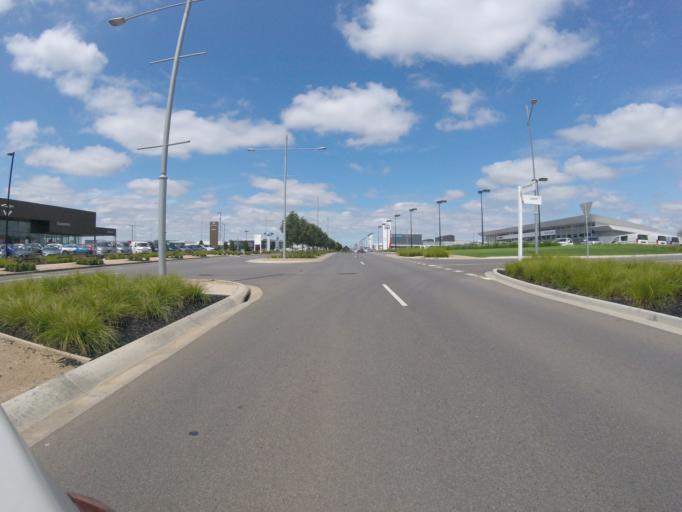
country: AU
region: Victoria
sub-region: Moreland
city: Gowanbrae
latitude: -37.7165
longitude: 144.8947
